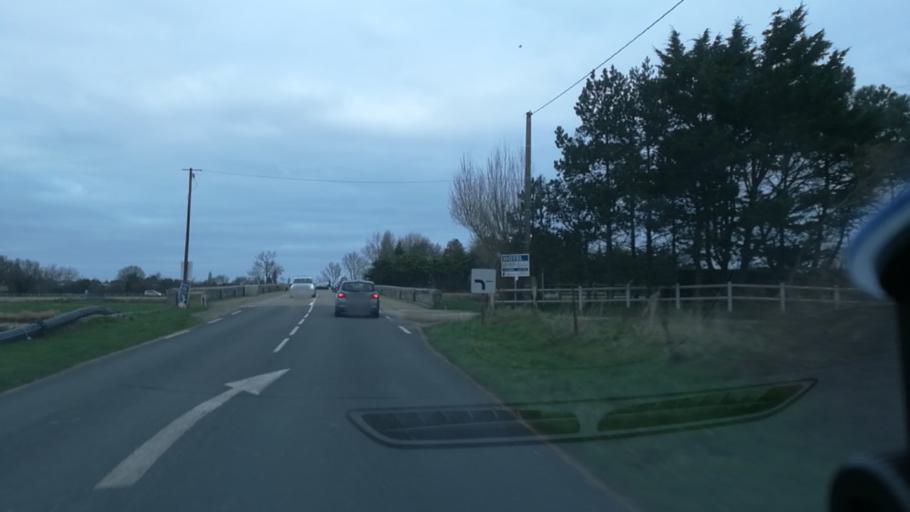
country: FR
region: Lower Normandy
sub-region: Departement de la Manche
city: Reville
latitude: 49.6114
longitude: -1.2564
